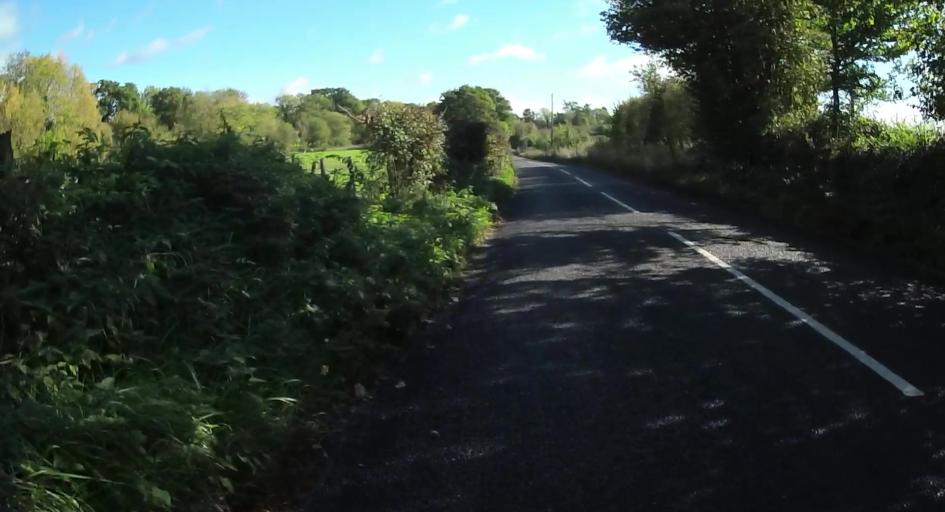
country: GB
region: England
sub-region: Hampshire
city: Old Basing
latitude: 51.2638
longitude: -1.0051
